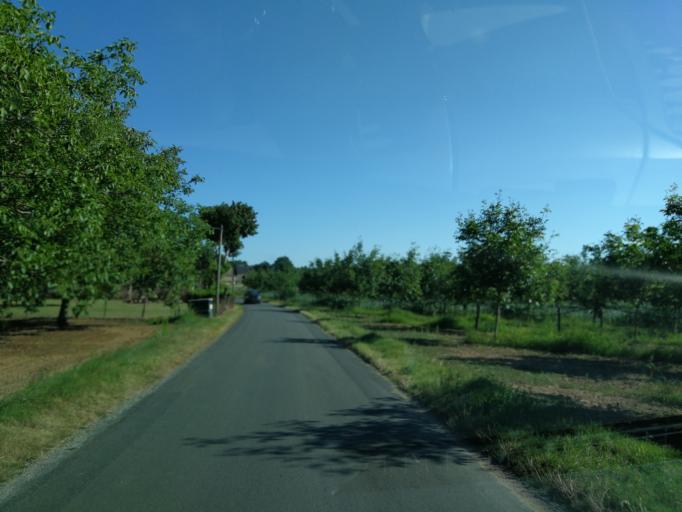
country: FR
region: Midi-Pyrenees
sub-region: Departement du Lot
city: Gourdon
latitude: 44.8293
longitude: 1.3606
